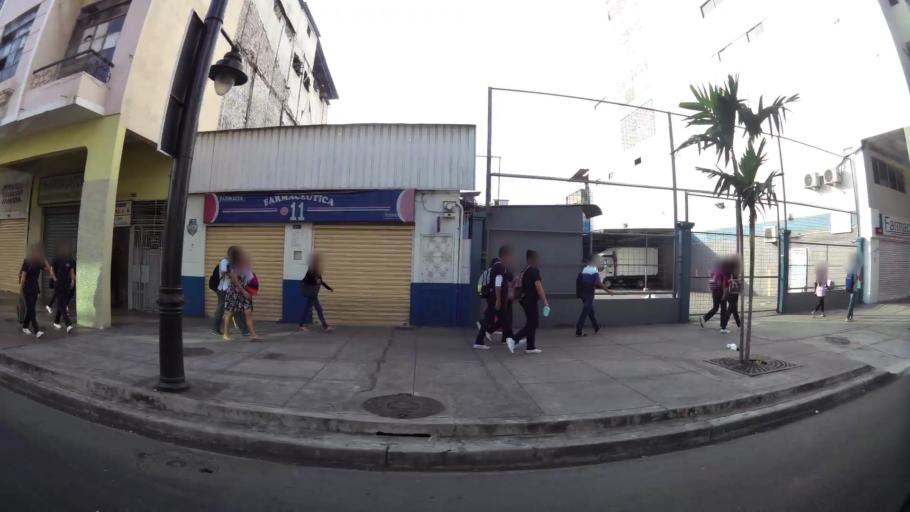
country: EC
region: Guayas
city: Eloy Alfaro
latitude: -2.1874
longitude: -79.8832
